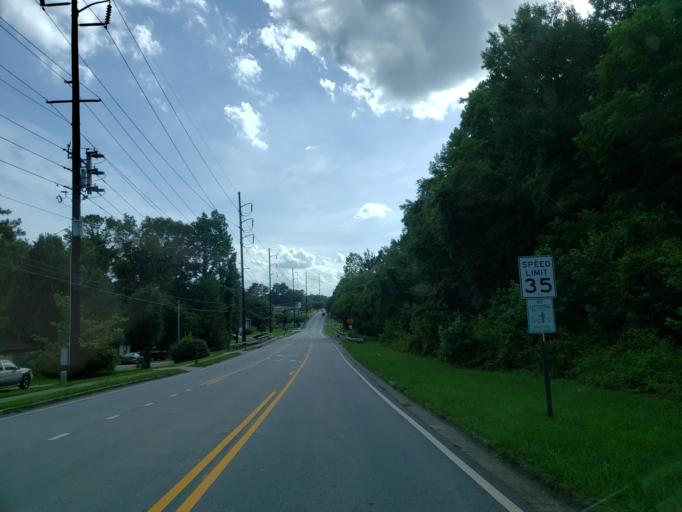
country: US
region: Georgia
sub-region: Cobb County
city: Powder Springs
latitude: 33.8766
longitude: -84.6594
